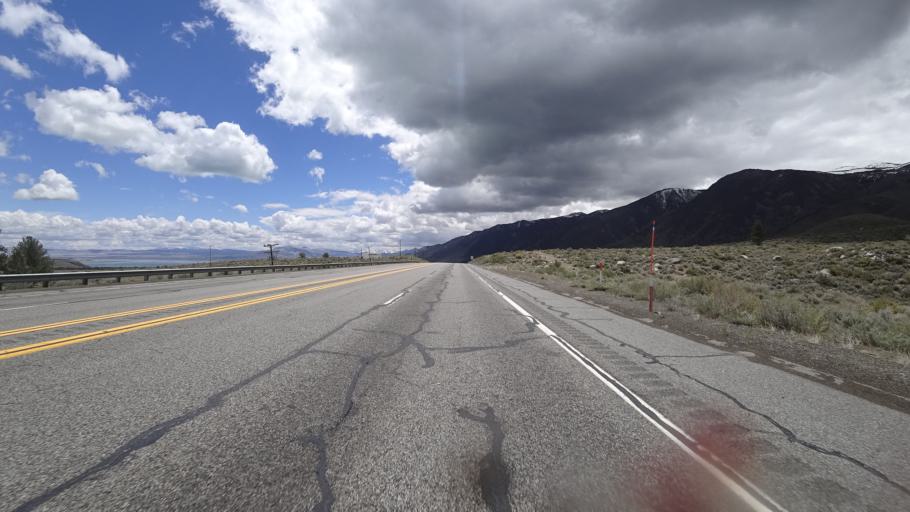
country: US
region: California
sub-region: Mono County
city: Bridgeport
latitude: 38.0399
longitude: -119.1587
